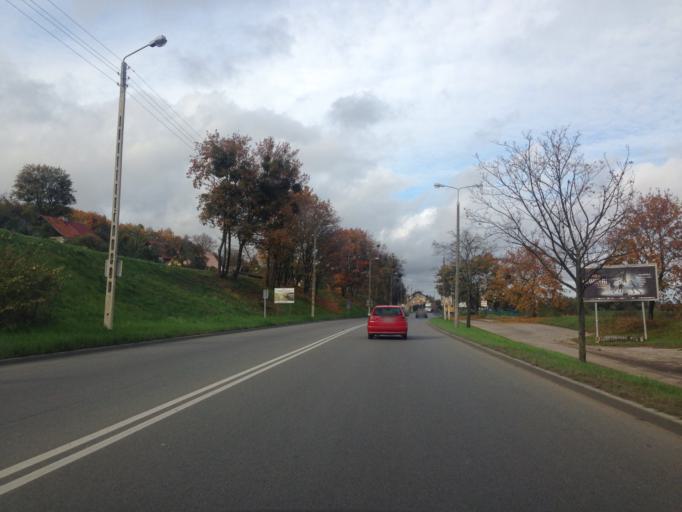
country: PL
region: Pomeranian Voivodeship
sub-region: Powiat gdanski
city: Pruszcz Gdanski
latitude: 54.2802
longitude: 18.6392
